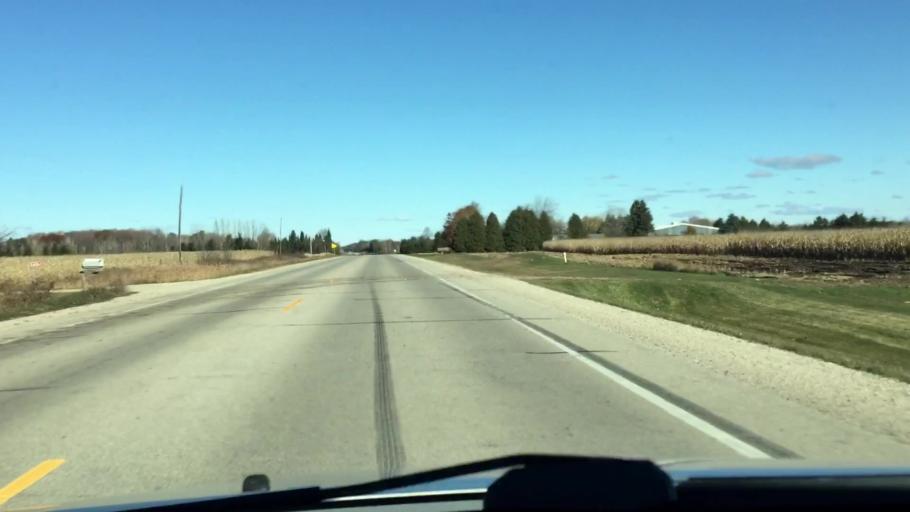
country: US
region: Wisconsin
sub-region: Brown County
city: Pulaski
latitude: 44.7393
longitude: -88.2479
